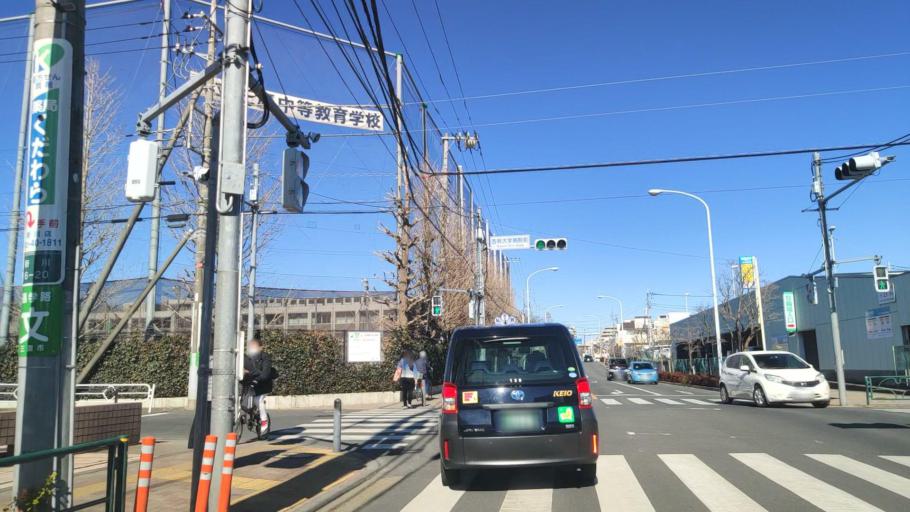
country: JP
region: Tokyo
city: Mitaka-shi
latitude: 35.6782
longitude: 139.5678
